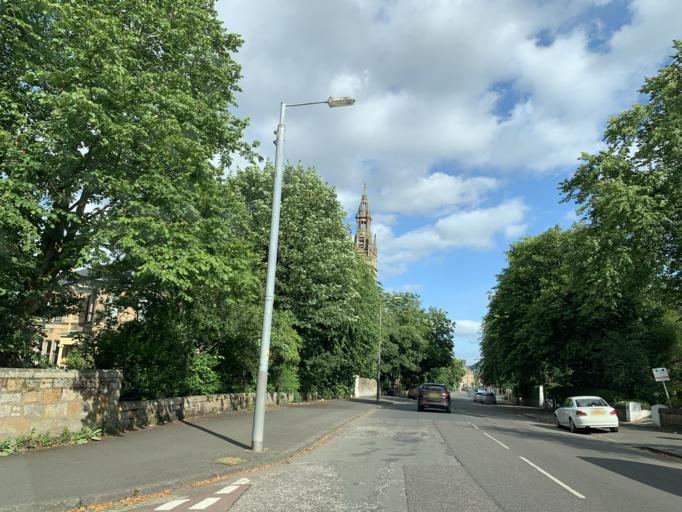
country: GB
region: Scotland
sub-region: Glasgow City
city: Glasgow
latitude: 55.8410
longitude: -4.2795
